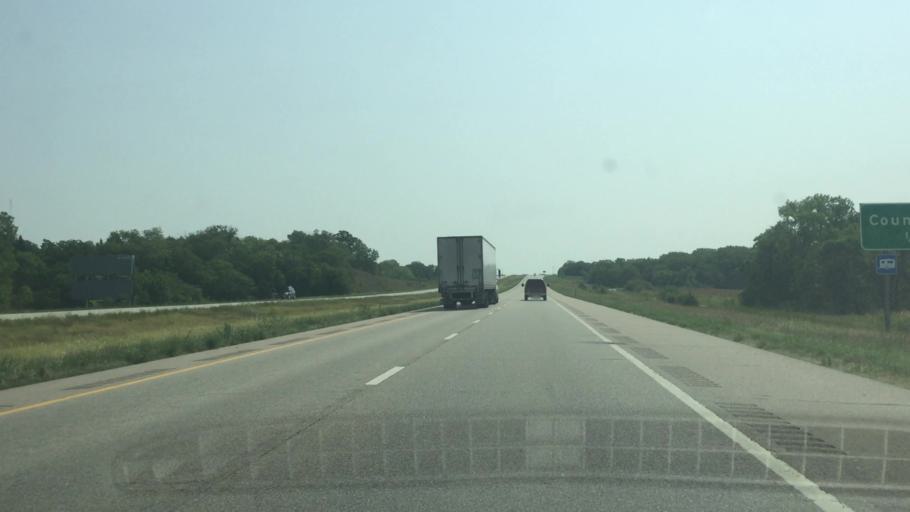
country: US
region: Kansas
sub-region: Lyon County
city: Emporia
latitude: 38.4108
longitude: -96.1077
